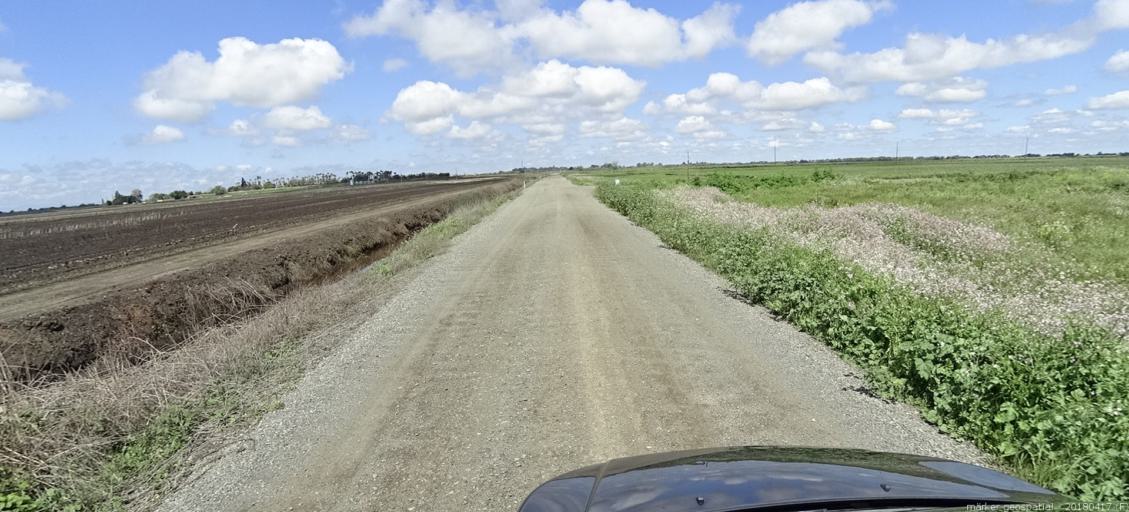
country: US
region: California
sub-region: Solano County
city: Rio Vista
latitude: 38.1404
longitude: -121.5818
